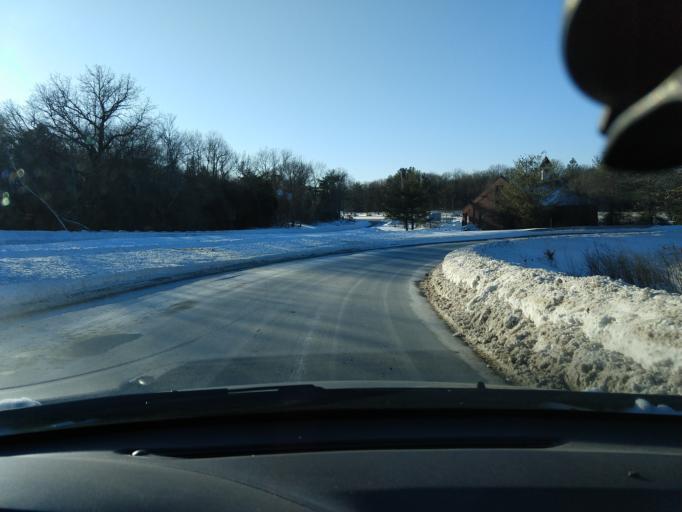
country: US
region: Massachusetts
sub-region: Middlesex County
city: Lexington
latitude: 42.4682
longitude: -71.2459
